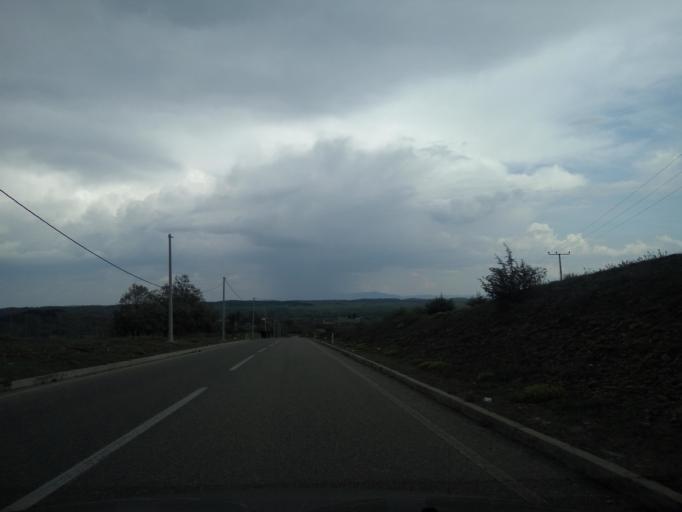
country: XK
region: Gjakova
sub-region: Komuna e Junikut
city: Junik
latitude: 42.4017
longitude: 20.2689
